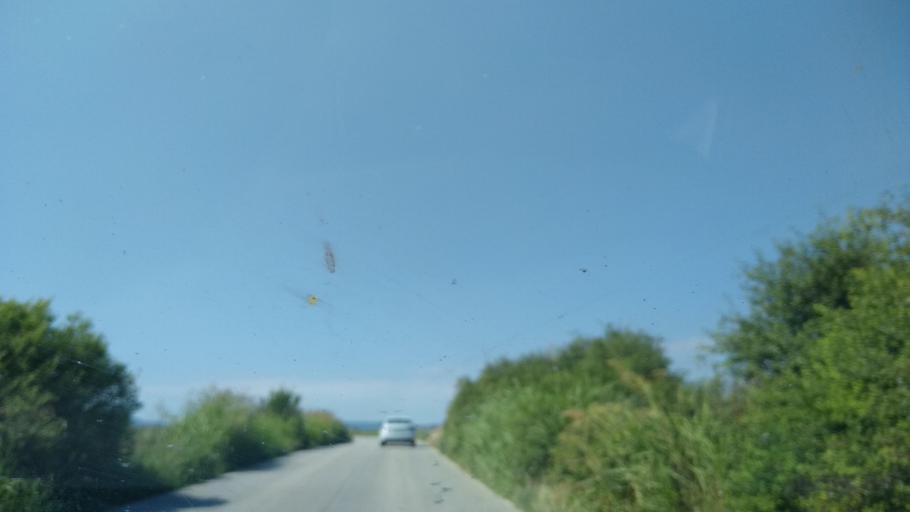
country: GR
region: Central Macedonia
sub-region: Nomos Thessalonikis
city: Nea Apollonia
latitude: 40.6232
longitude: 23.4658
